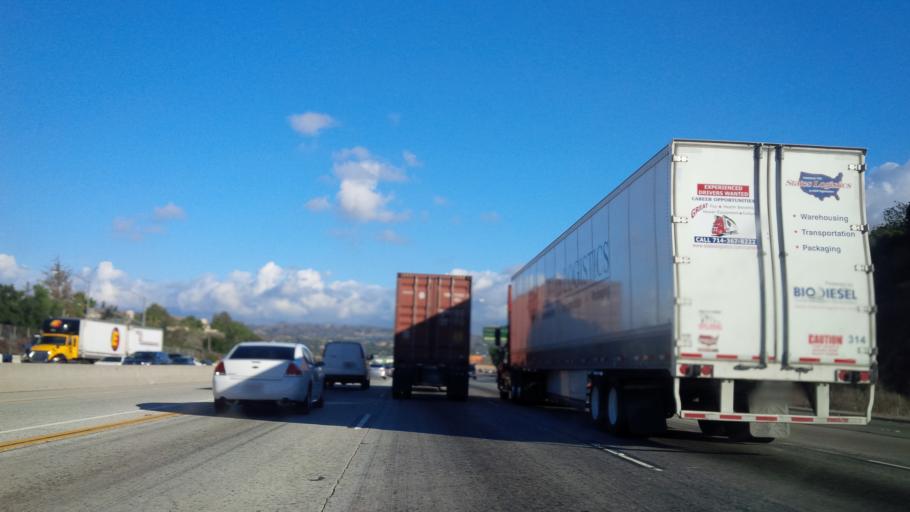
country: US
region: California
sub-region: Los Angeles County
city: Walnut
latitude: 33.9888
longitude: -117.8428
